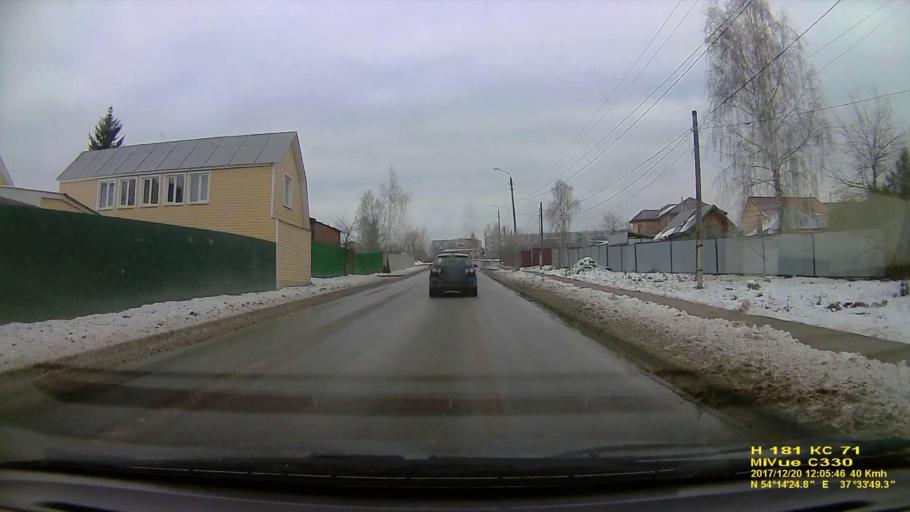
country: RU
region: Tula
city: Gorelki
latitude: 54.2403
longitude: 37.5637
